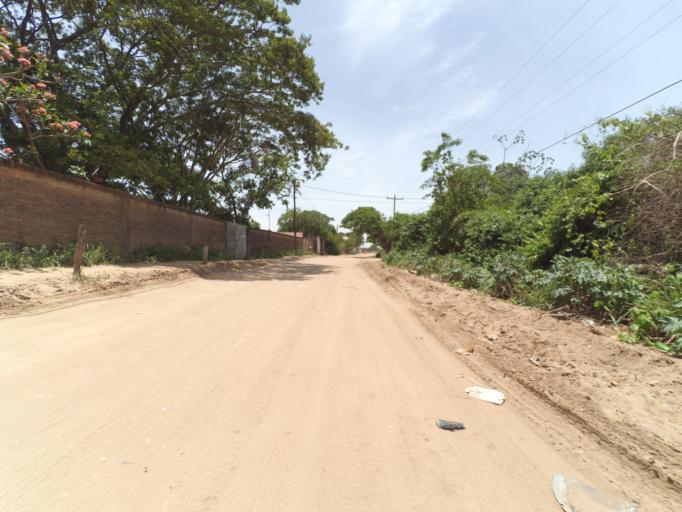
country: BO
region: Santa Cruz
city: Santa Cruz de la Sierra
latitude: -17.8231
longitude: -63.2485
